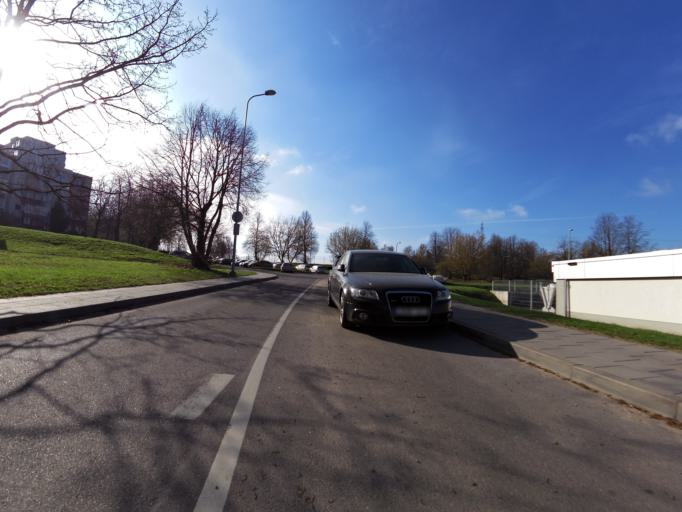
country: LT
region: Vilnius County
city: Seskine
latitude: 54.7119
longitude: 25.2409
